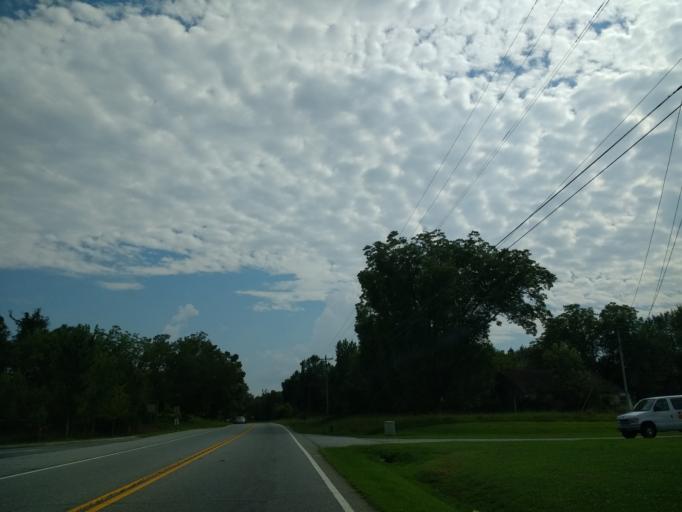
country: US
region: Georgia
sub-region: Hall County
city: Gainesville
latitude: 34.3911
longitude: -83.8053
